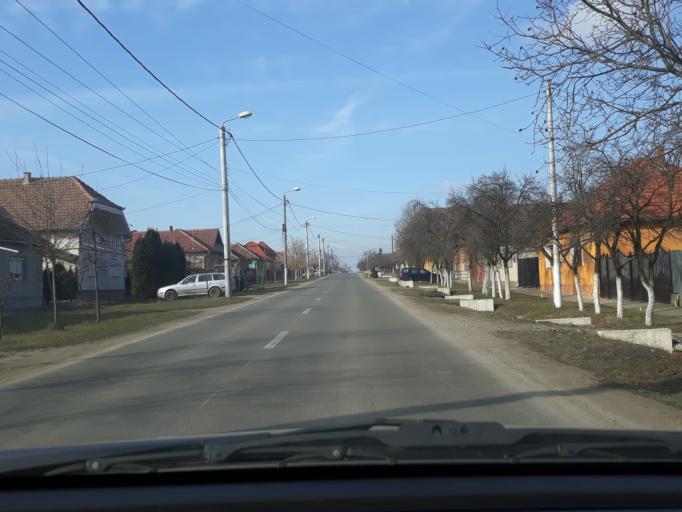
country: RO
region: Bihor
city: Margita
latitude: 47.3551
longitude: 22.3375
